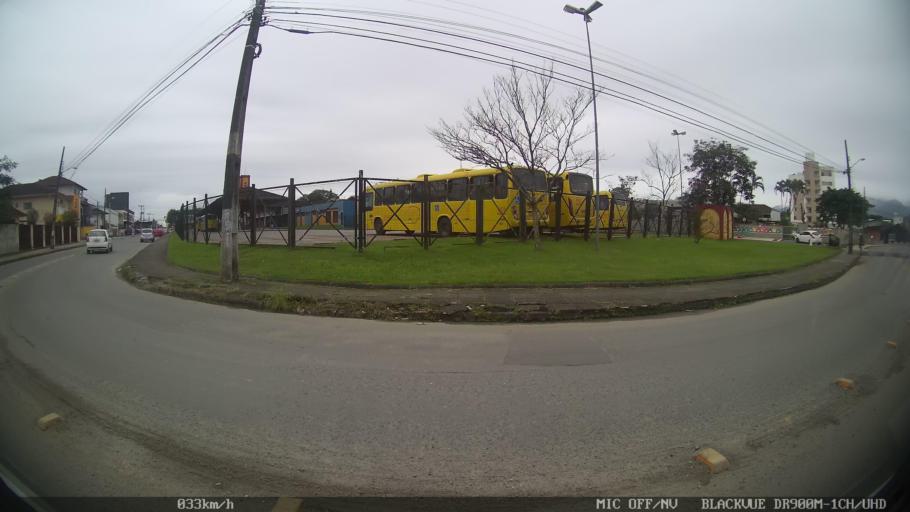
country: BR
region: Santa Catarina
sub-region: Joinville
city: Joinville
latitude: -26.2856
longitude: -48.9027
